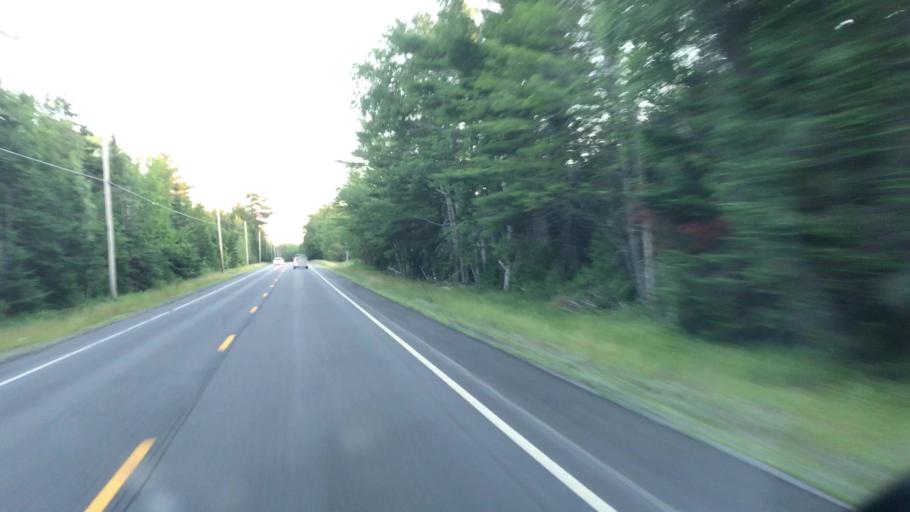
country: US
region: Maine
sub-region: Penobscot County
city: Medway
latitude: 45.5824
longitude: -68.3169
